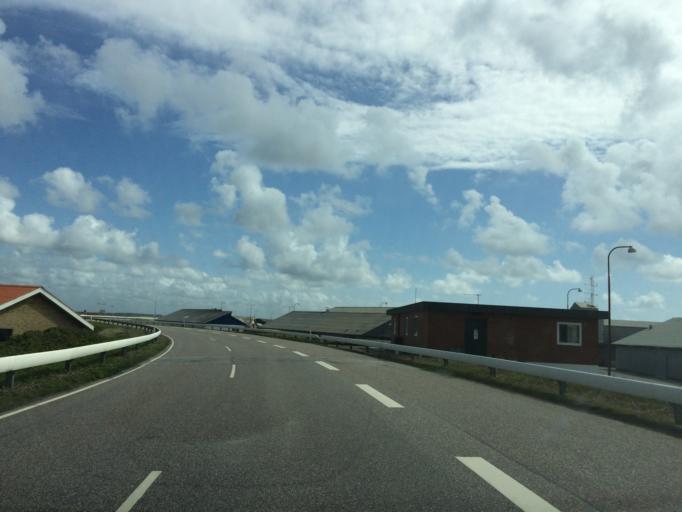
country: DK
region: Central Jutland
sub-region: Holstebro Kommune
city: Ulfborg
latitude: 56.3704
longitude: 8.1209
